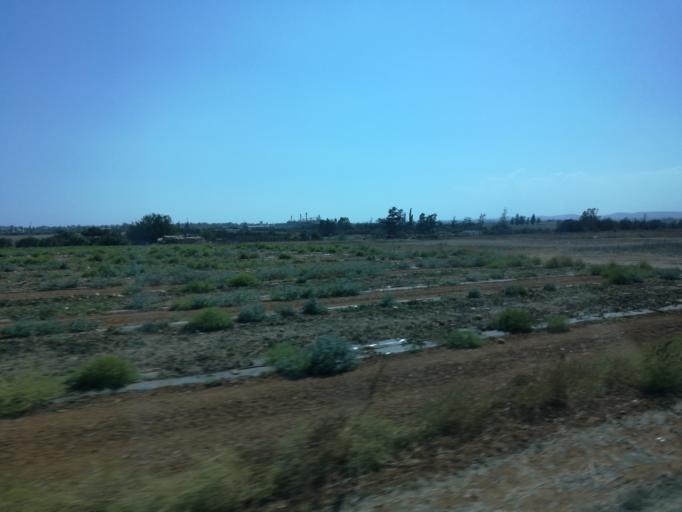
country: CY
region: Ammochostos
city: Achna
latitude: 35.0469
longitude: 33.7772
